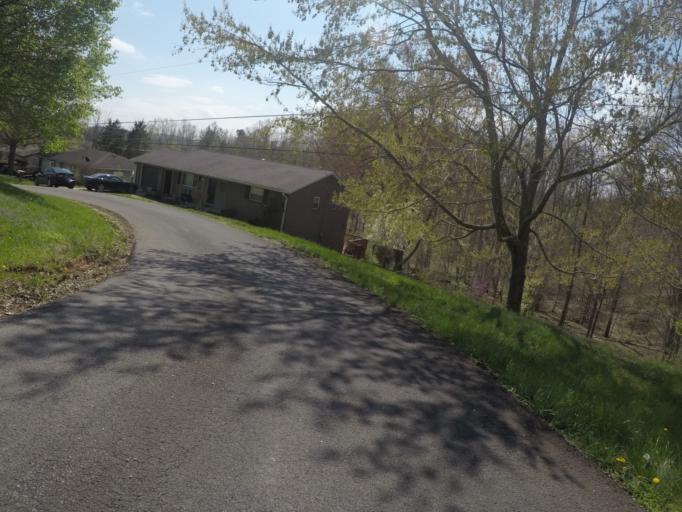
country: US
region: Ohio
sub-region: Lawrence County
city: Burlington
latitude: 38.3805
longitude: -82.5308
